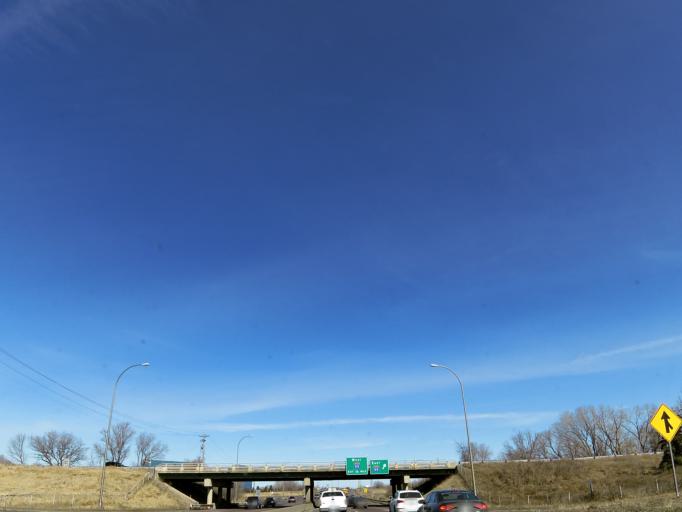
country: US
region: Minnesota
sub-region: Hennepin County
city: Minnetonka Mills
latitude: 44.9783
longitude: -93.4004
